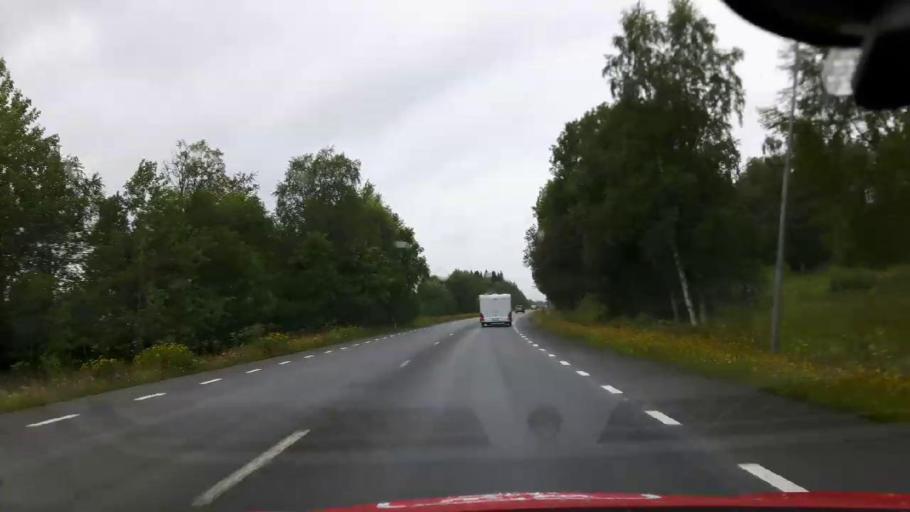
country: SE
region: Jaemtland
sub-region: Are Kommun
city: Jarpen
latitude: 63.3112
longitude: 13.6057
